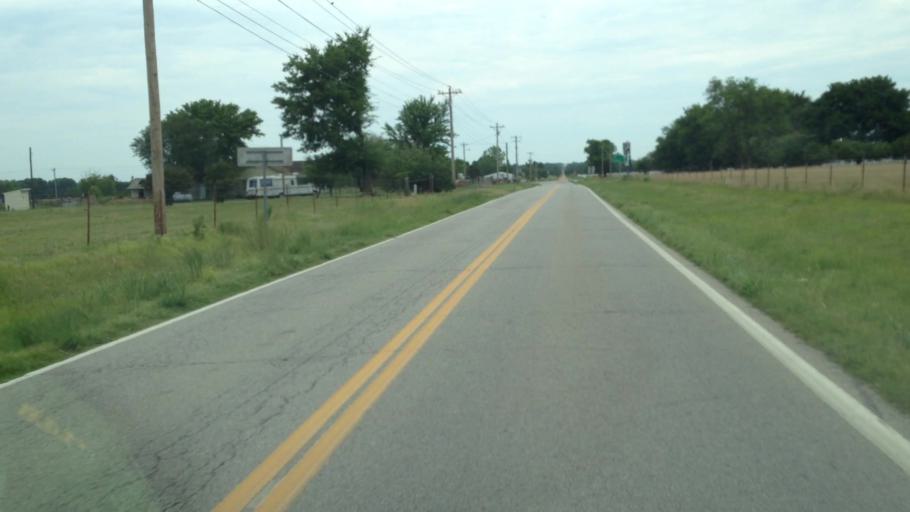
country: US
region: Oklahoma
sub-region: Delaware County
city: Cleora
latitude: 36.6101
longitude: -94.9634
